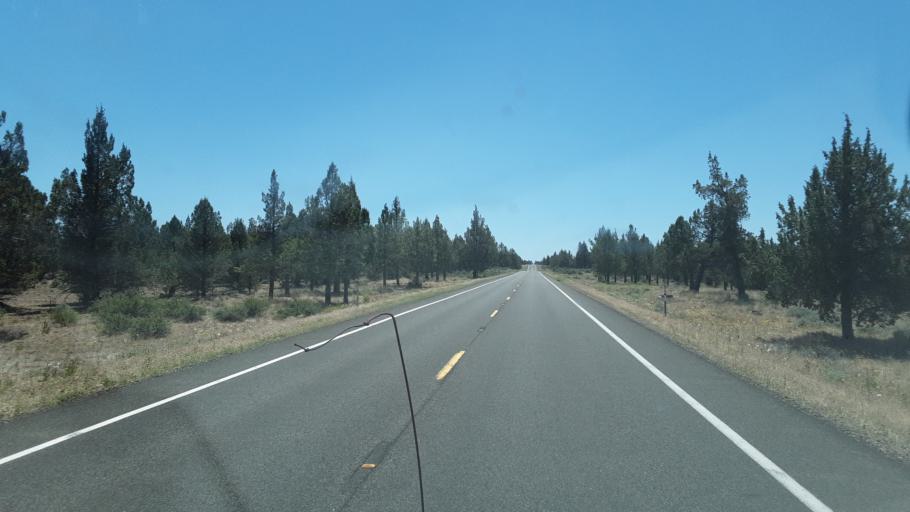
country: US
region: California
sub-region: Siskiyou County
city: Tulelake
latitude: 41.6566
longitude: -121.2466
